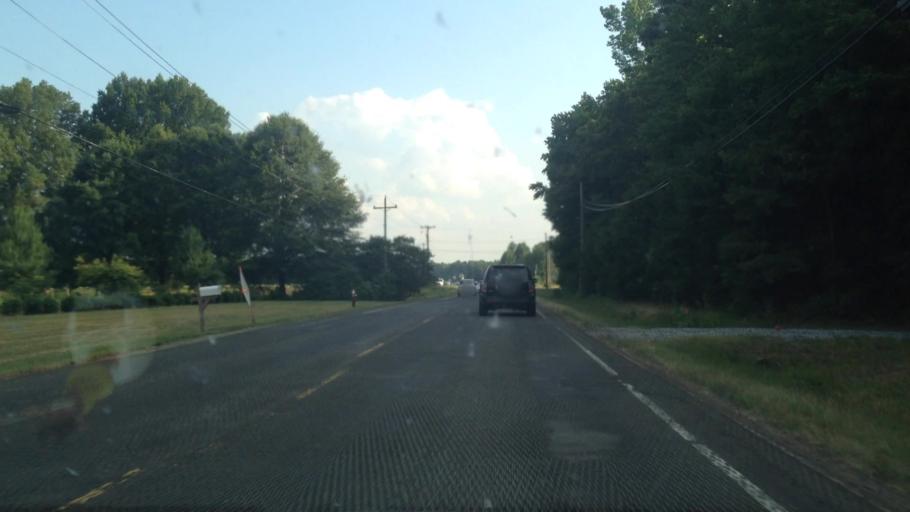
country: US
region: North Carolina
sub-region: Davidson County
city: Wallburg
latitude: 36.0318
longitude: -80.0561
